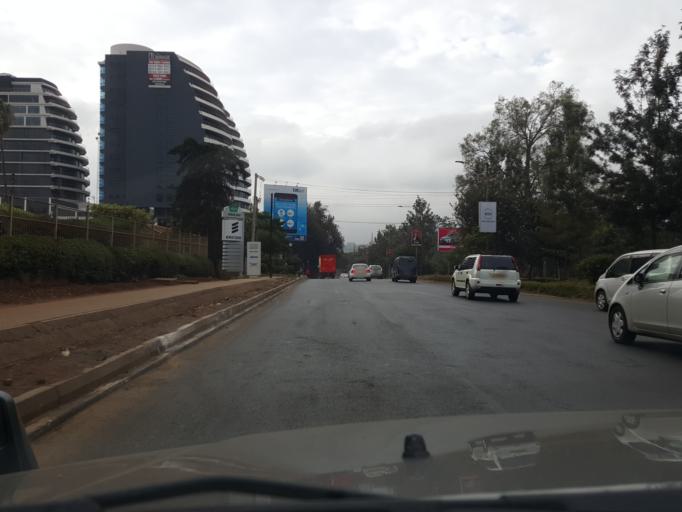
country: KE
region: Nairobi Area
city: Nairobi
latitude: -1.2687
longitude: 36.8059
